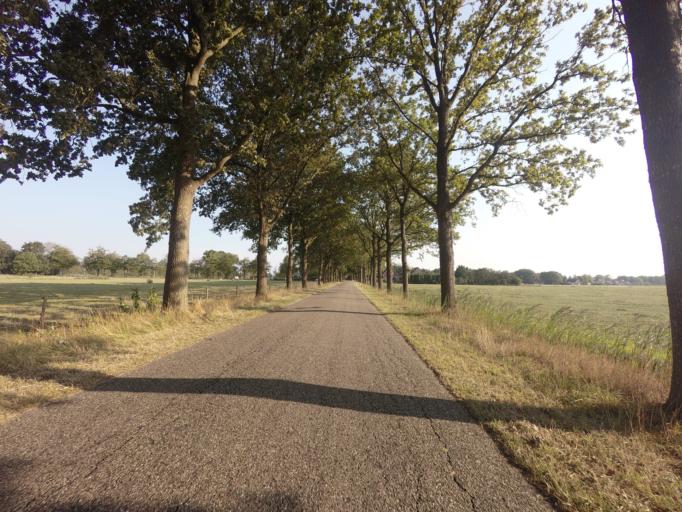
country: NL
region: Drenthe
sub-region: Gemeente Tynaarlo
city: Vries
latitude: 53.1351
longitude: 6.4897
